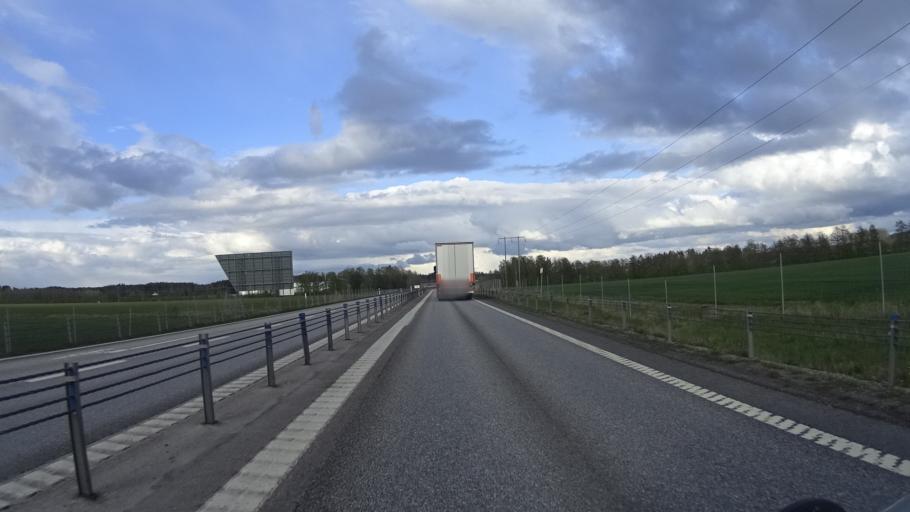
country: SE
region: Vaestmanland
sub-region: Hallstahammars Kommun
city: Hallstahammar
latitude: 59.5904
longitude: 16.2230
